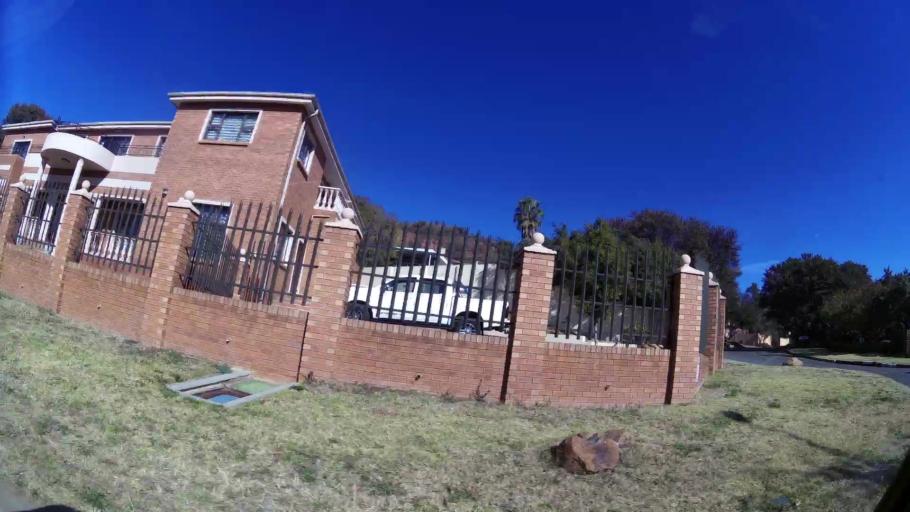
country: ZA
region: Gauteng
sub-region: City of Johannesburg Metropolitan Municipality
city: Johannesburg
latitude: -26.2786
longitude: 28.0212
